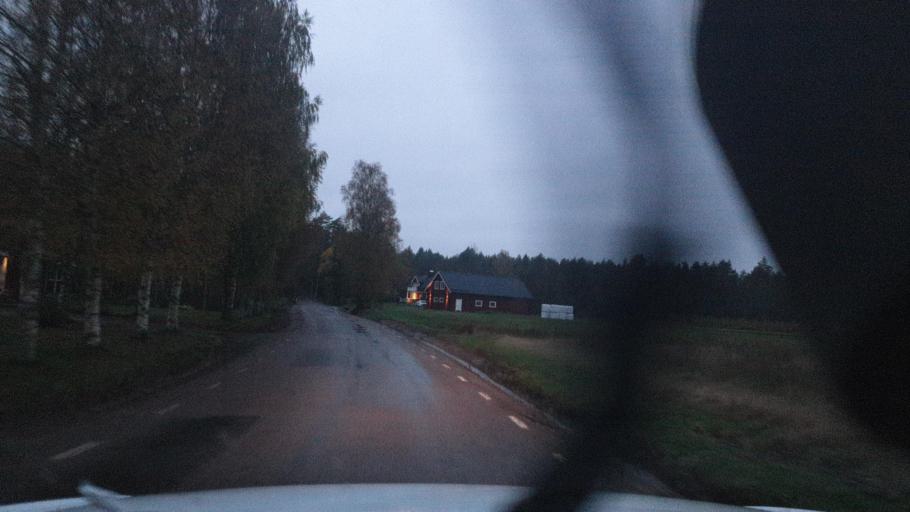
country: SE
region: Vaermland
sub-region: Eda Kommun
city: Charlottenberg
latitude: 59.8617
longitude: 12.3446
